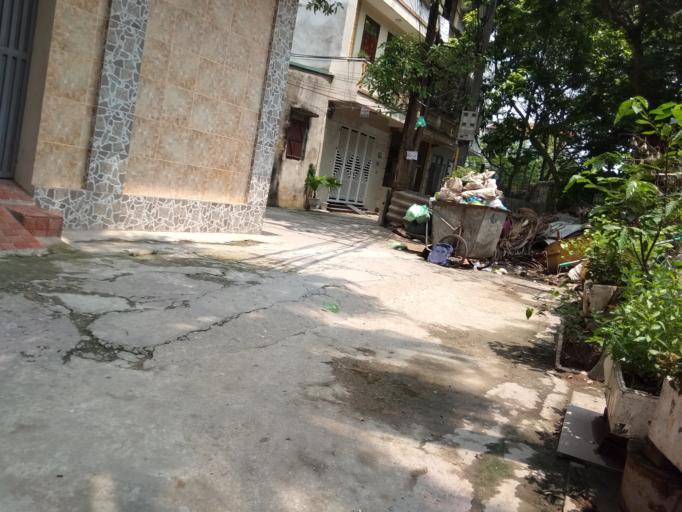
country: VN
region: Ha Noi
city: Cau Giay
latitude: 21.0508
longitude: 105.8031
